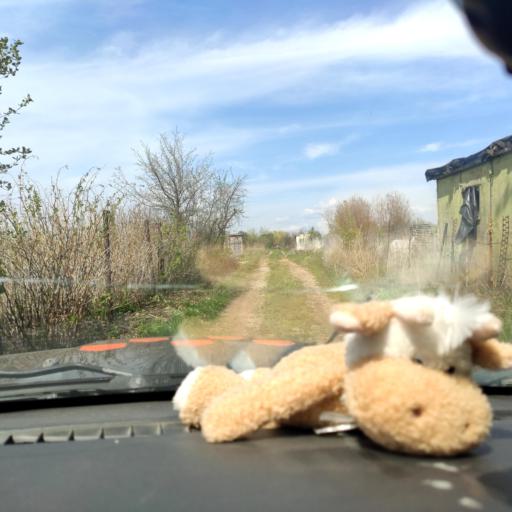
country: RU
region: Samara
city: Podstepki
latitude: 53.5106
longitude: 49.0853
